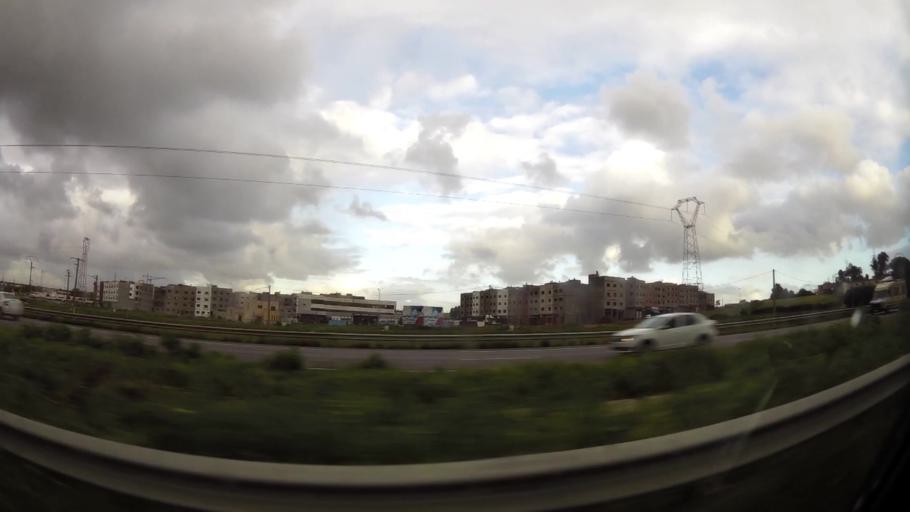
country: MA
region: Grand Casablanca
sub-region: Mohammedia
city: Mohammedia
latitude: 33.6348
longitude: -7.4228
